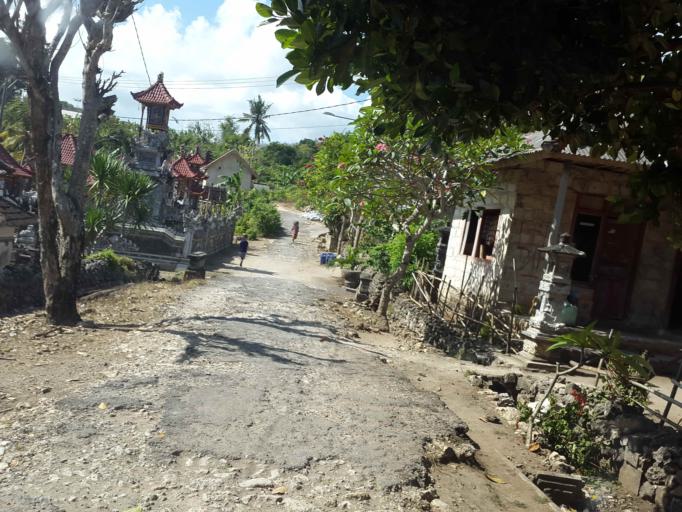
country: ID
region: Bali
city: Pondokkaha Kelod
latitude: -8.7521
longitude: 115.4912
